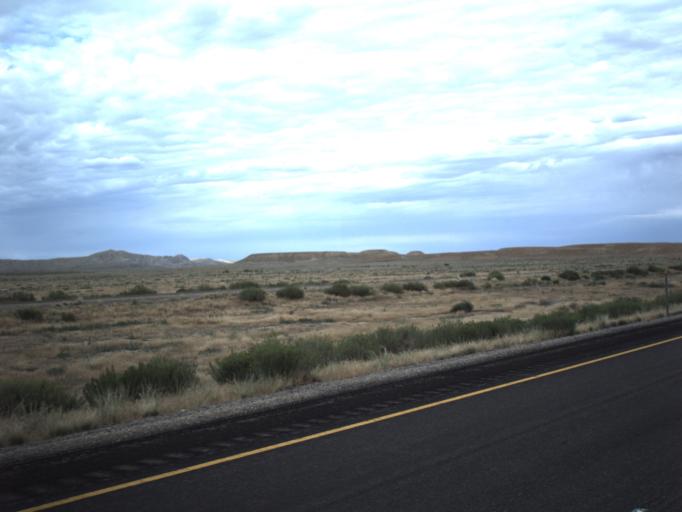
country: US
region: Utah
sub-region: Grand County
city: Moab
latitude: 38.9446
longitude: -109.6475
